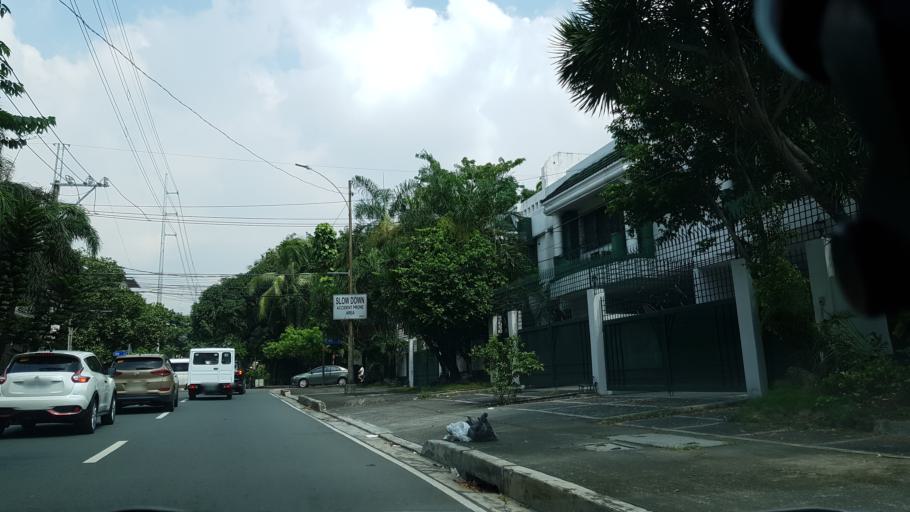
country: PH
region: Metro Manila
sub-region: San Juan
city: San Juan
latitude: 14.6178
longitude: 121.0353
